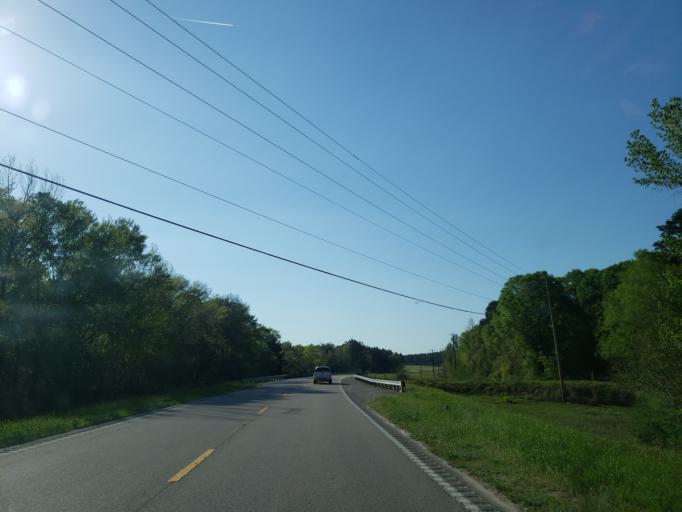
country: US
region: Mississippi
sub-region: Perry County
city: Richton
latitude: 31.4711
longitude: -88.9990
